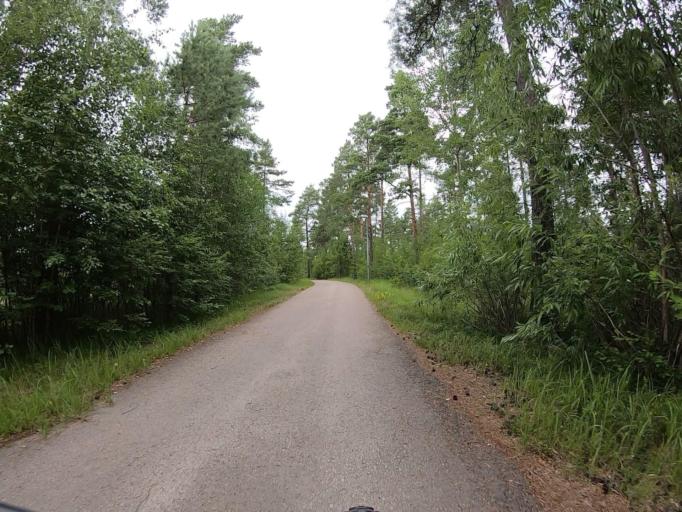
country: FI
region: Varsinais-Suomi
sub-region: Vakka-Suomi
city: Uusikaupunki
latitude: 60.8166
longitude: 21.4167
